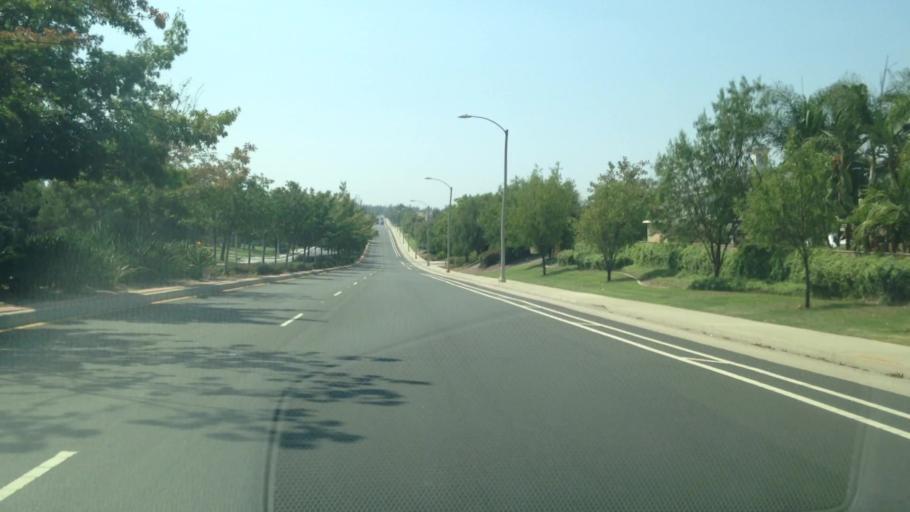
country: US
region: California
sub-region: Riverside County
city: Woodcrest
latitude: 33.9125
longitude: -117.3302
